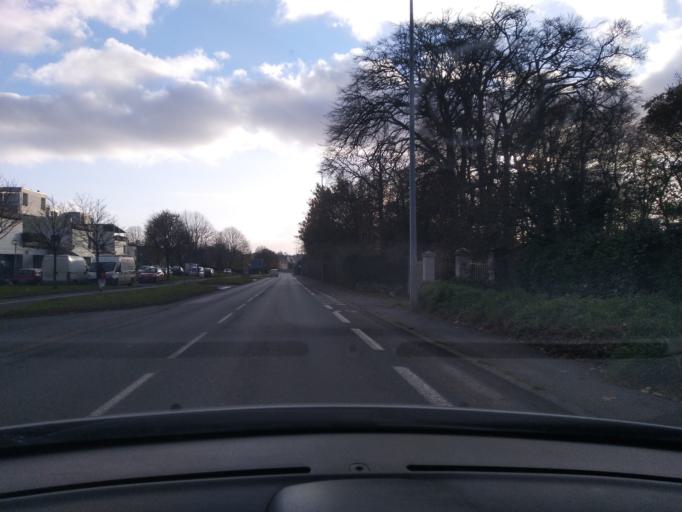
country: FR
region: Brittany
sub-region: Departement du Finistere
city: Morlaix
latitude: 48.5866
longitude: -3.8150
